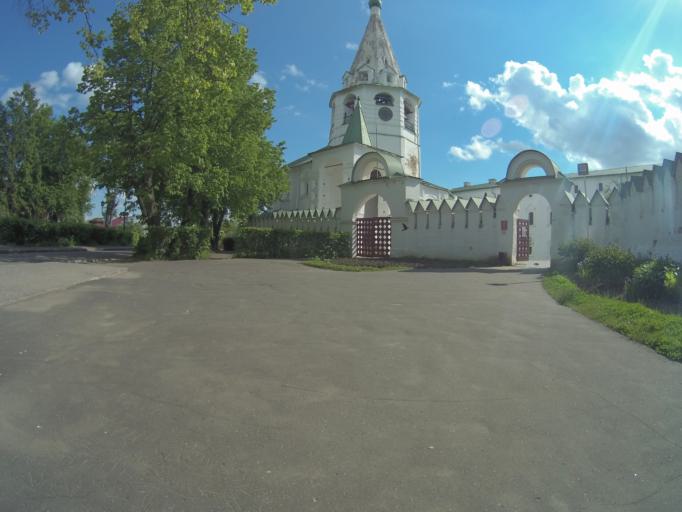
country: RU
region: Vladimir
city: Suzdal'
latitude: 56.4168
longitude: 40.4435
